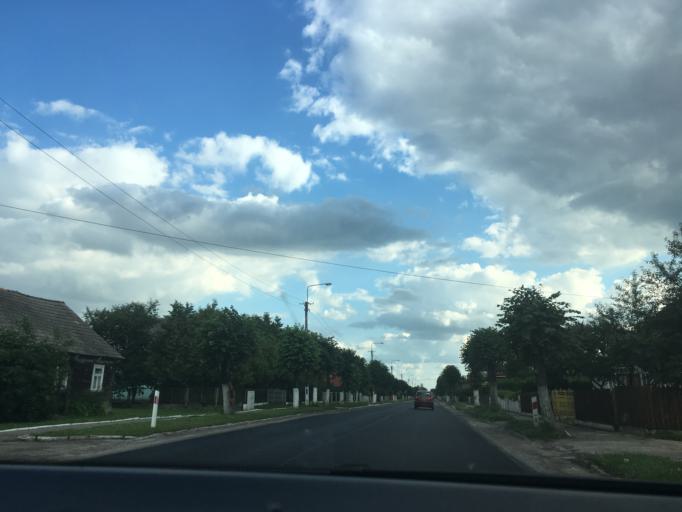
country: PL
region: Podlasie
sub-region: Powiat bielski
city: Bielsk Podlaski
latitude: 52.8088
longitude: 23.1944
